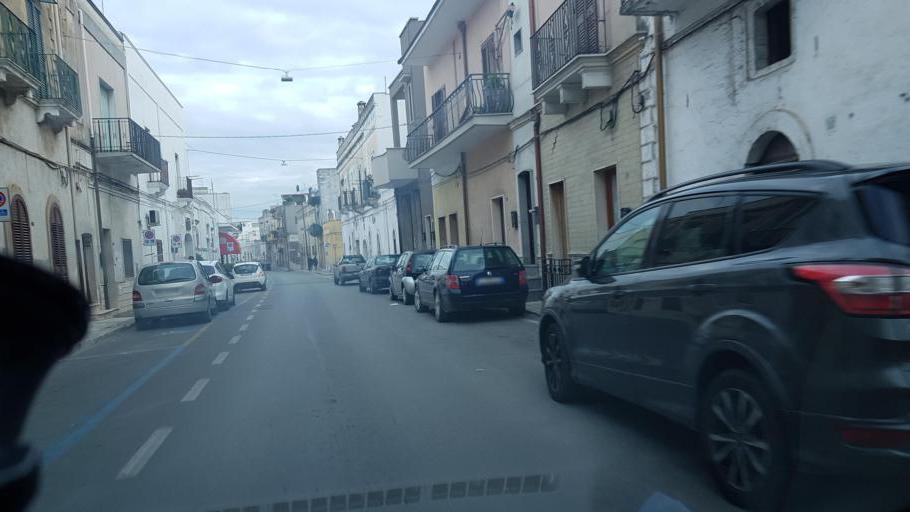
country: IT
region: Apulia
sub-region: Provincia di Brindisi
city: Oria
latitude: 40.4966
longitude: 17.6403
